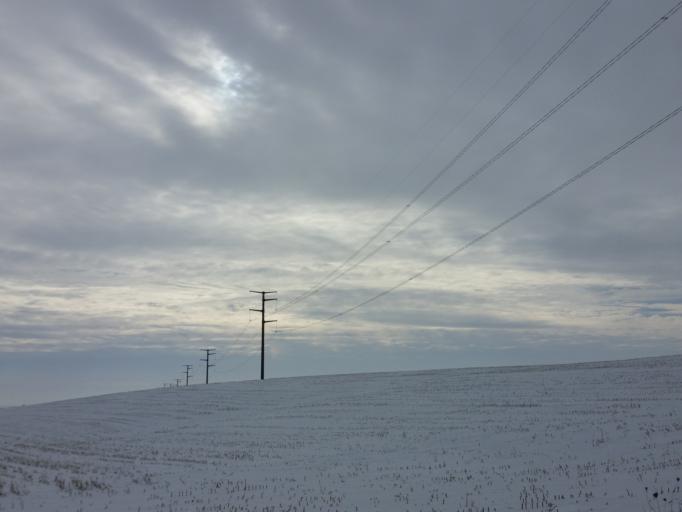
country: US
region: Iowa
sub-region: Dubuque County
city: Peosta
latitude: 42.3967
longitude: -90.8396
